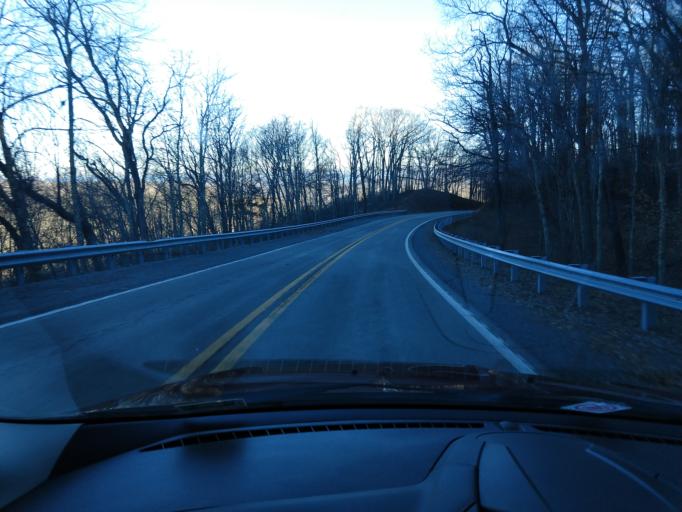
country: US
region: Virginia
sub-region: Highland County
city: Monterey
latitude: 38.4842
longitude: -79.7030
